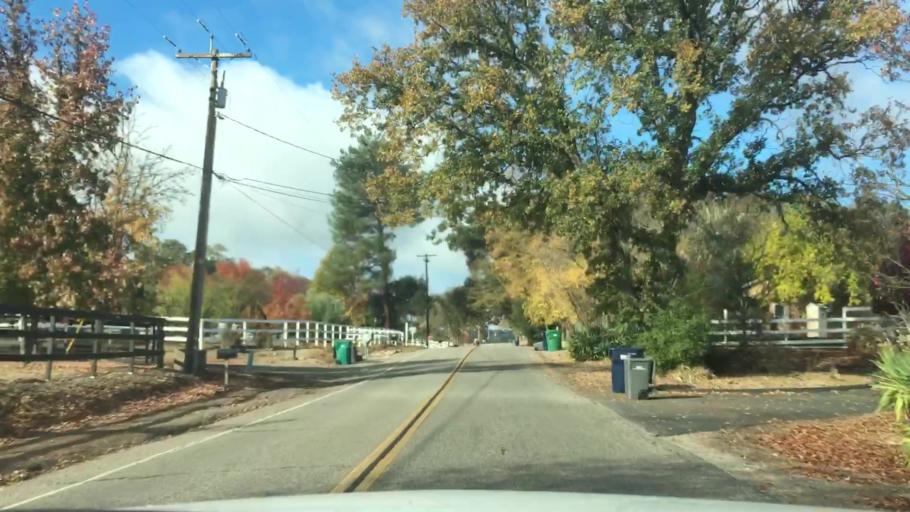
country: US
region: California
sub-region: San Luis Obispo County
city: Atascadero
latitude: 35.4582
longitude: -120.6625
